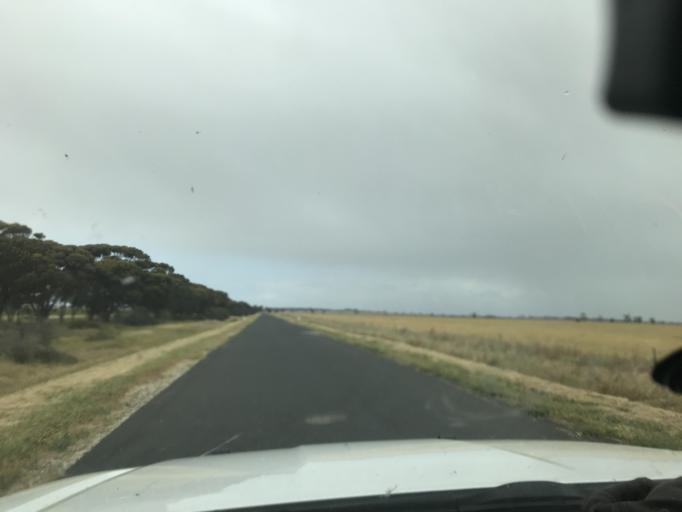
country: AU
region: South Australia
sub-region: Tatiara
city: Bordertown
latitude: -36.4161
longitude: 141.1764
